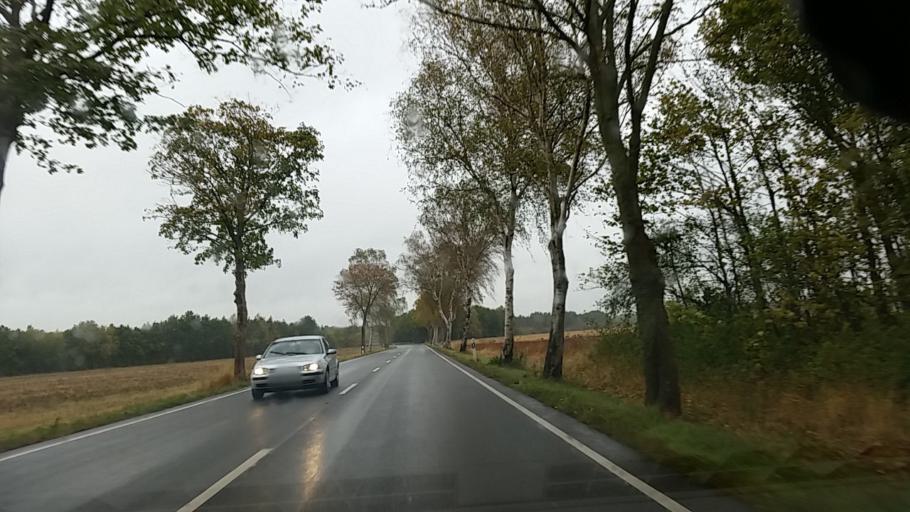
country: DE
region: Lower Saxony
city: Wrestedt
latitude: 52.9227
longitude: 10.6124
